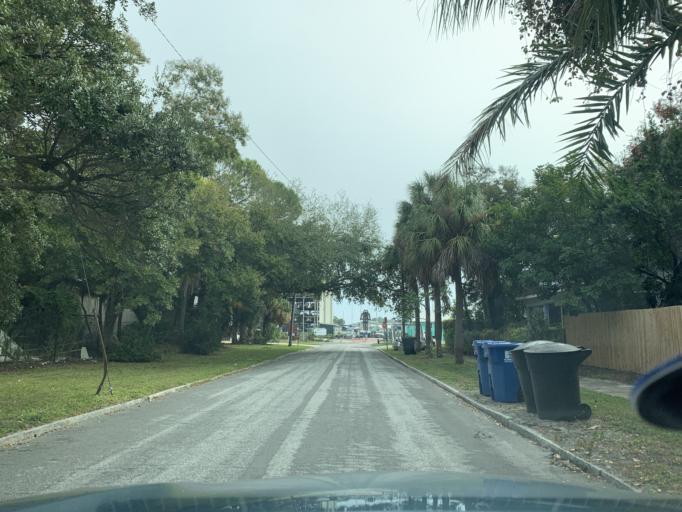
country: US
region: Florida
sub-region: Pinellas County
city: Saint Petersburg
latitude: 27.7558
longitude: -82.6363
